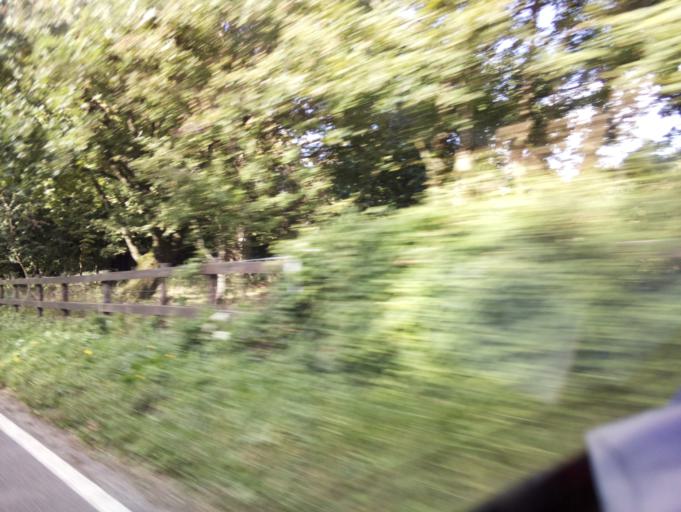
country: GB
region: England
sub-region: Hampshire
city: Basingstoke
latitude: 51.2151
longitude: -1.0570
